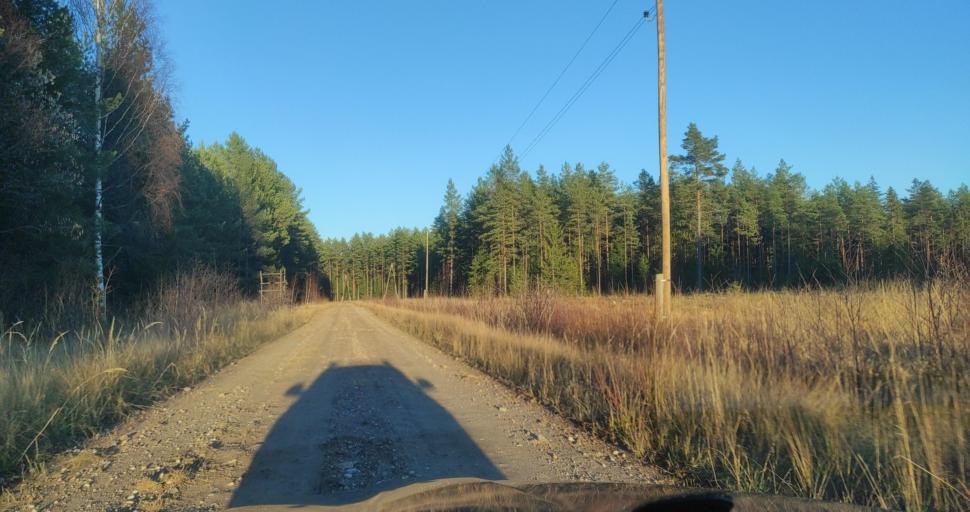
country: LV
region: Dundaga
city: Dundaga
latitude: 57.3716
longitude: 22.0754
